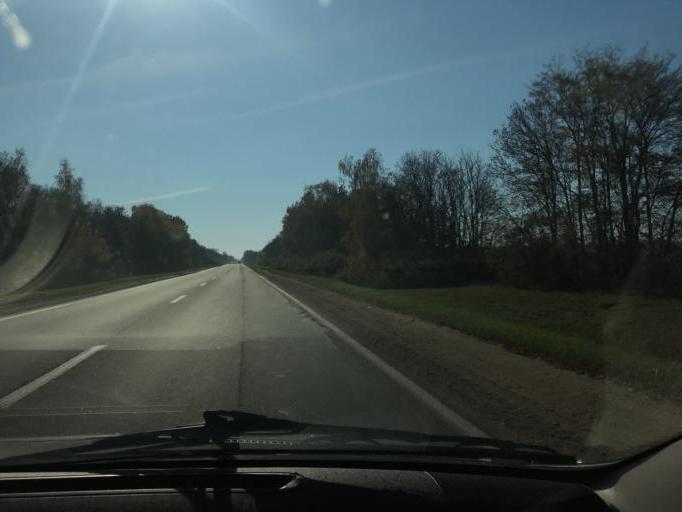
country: BY
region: Minsk
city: Starobin
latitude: 52.7925
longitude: 27.4646
